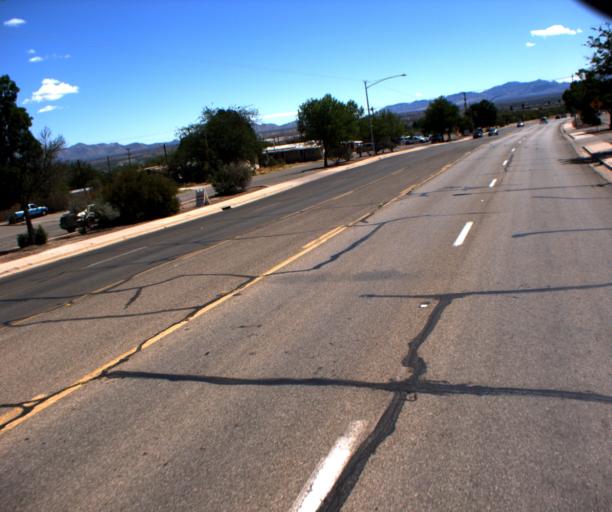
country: US
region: Arizona
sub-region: Cochise County
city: Benson
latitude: 31.9706
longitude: -110.3094
